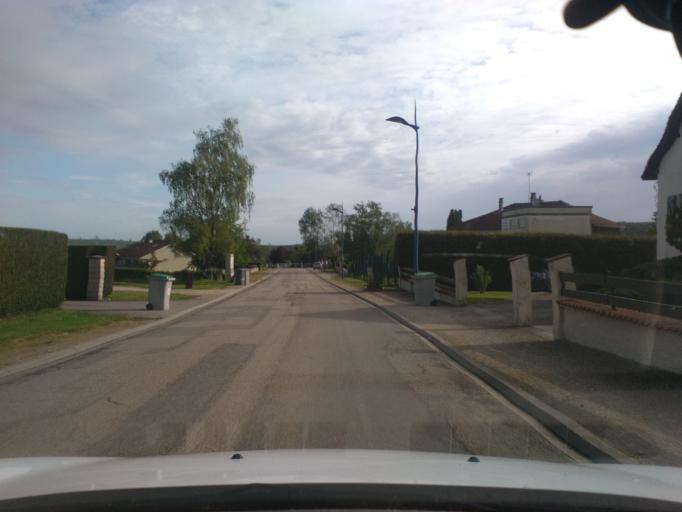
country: FR
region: Lorraine
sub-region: Departement des Vosges
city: Mirecourt
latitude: 48.3189
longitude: 6.1473
